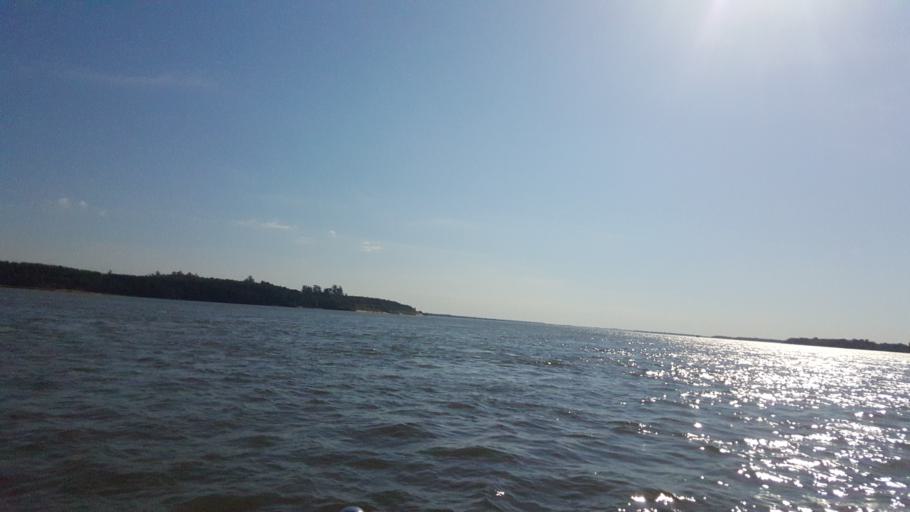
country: AR
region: Corrientes
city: Ituzaingo
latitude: -27.6034
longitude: -56.8510
